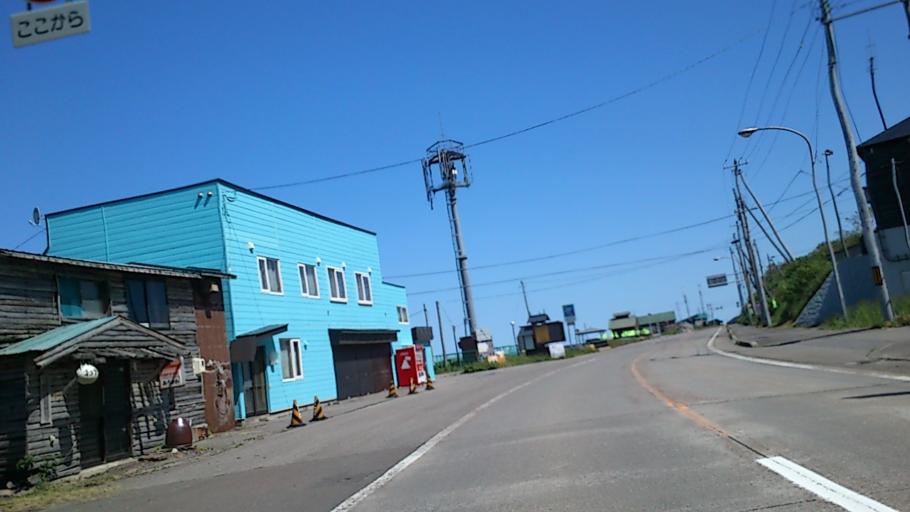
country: JP
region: Hokkaido
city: Rumoi
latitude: 43.7368
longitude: 141.3383
